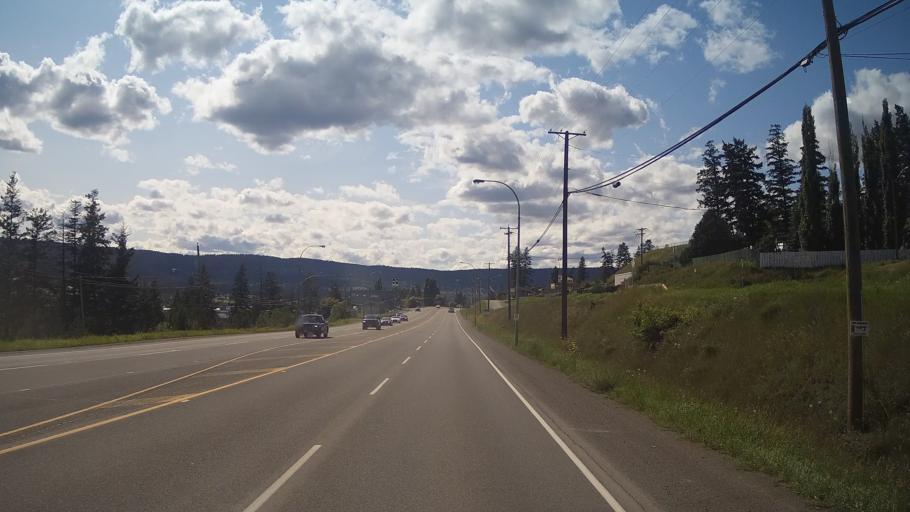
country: CA
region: British Columbia
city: Williams Lake
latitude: 52.1223
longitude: -122.1040
